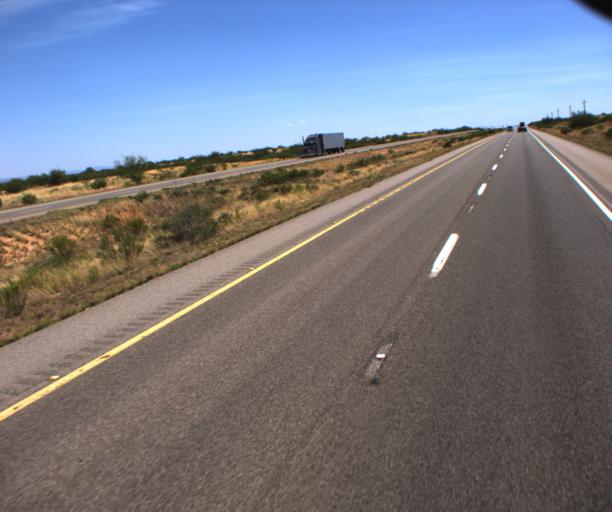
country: US
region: Arizona
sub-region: Cochise County
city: Whetstone
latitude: 31.8976
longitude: -110.3414
